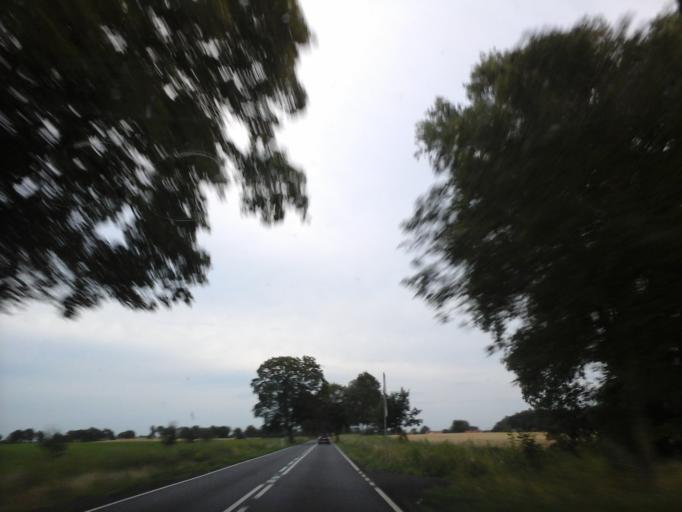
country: PL
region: West Pomeranian Voivodeship
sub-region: Powiat stargardzki
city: Stara Dabrowa
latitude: 53.4134
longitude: 15.0939
